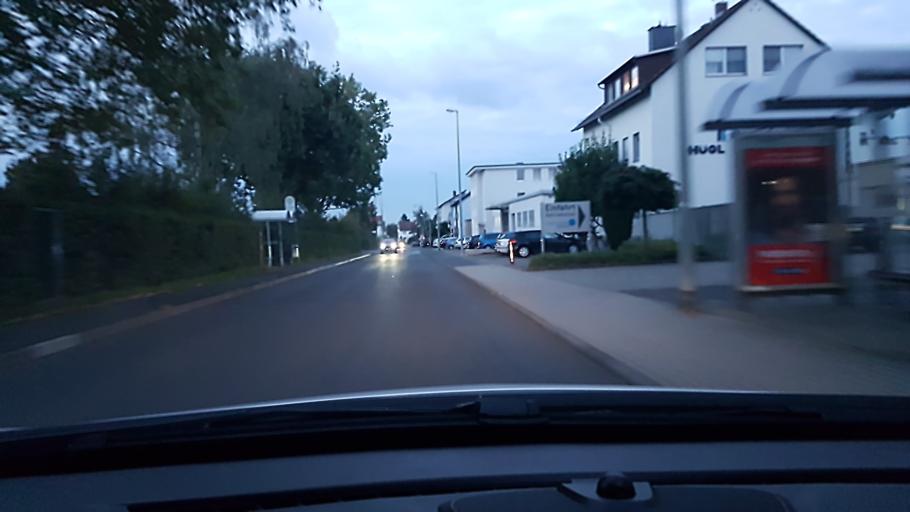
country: DE
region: Hesse
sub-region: Regierungsbezirk Darmstadt
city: Oberursel
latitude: 50.1882
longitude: 8.5932
